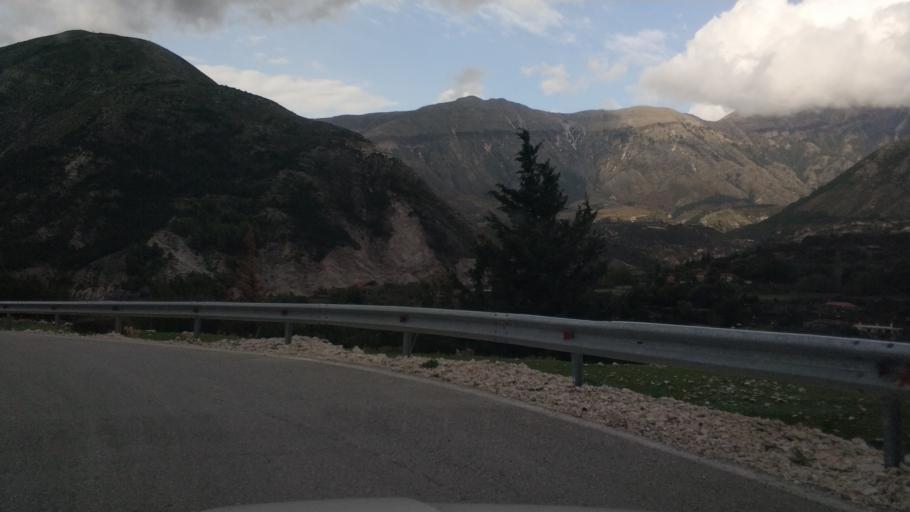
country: AL
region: Vlore
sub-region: Rrethi i Vlores
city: Orikum
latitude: 40.2415
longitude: 19.5515
